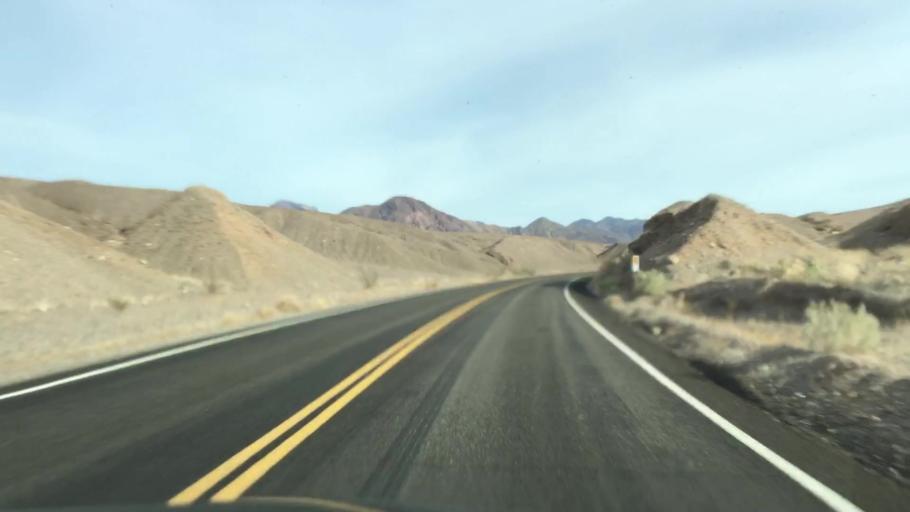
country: US
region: Nevada
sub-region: Nye County
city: Beatty
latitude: 36.6650
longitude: -117.0181
